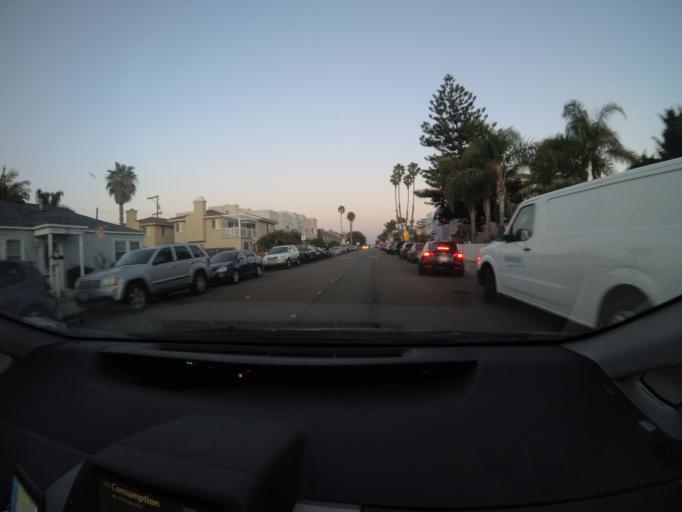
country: US
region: California
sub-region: San Diego County
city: Imperial Beach
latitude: 32.5802
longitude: -117.1309
